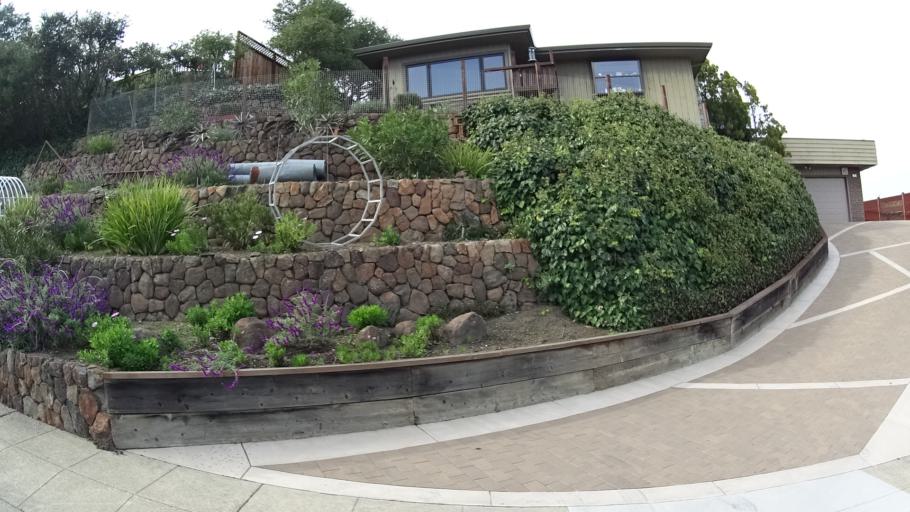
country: US
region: California
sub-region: San Mateo County
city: Hillsborough
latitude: 37.5756
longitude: -122.3821
